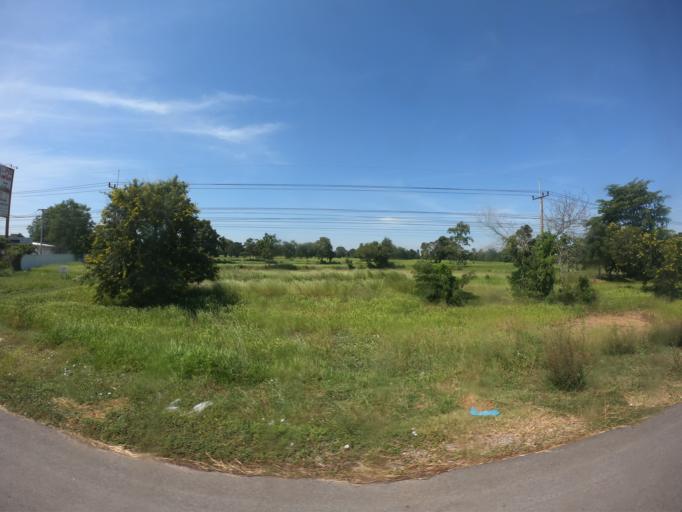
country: TH
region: Nakhon Ratchasima
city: Sida
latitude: 15.6213
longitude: 102.5659
